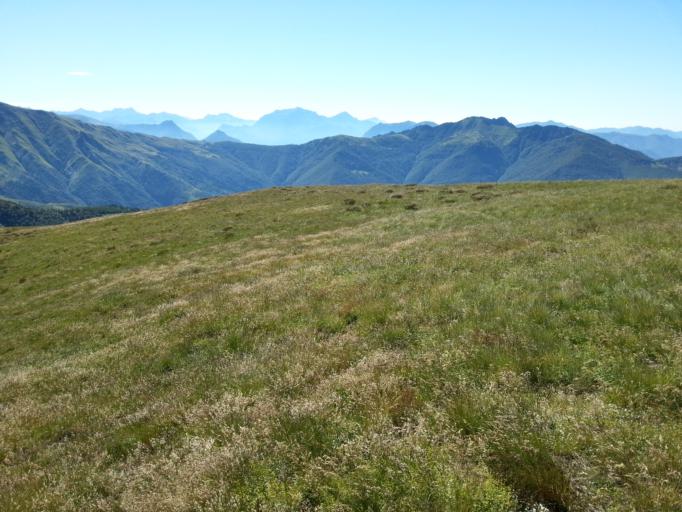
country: CH
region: Ticino
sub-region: Bellinzona District
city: Camorino
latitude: 46.1079
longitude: 9.0132
